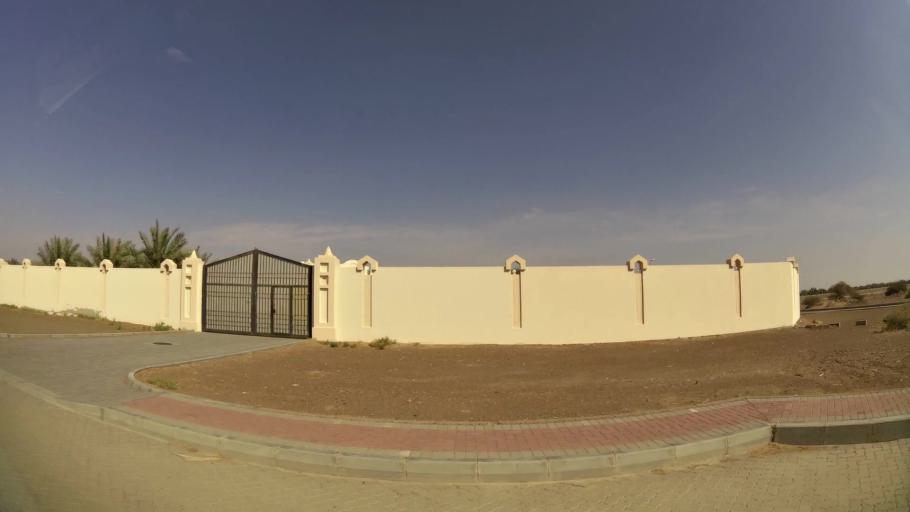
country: AE
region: Abu Dhabi
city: Al Ain
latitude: 24.0872
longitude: 55.9272
